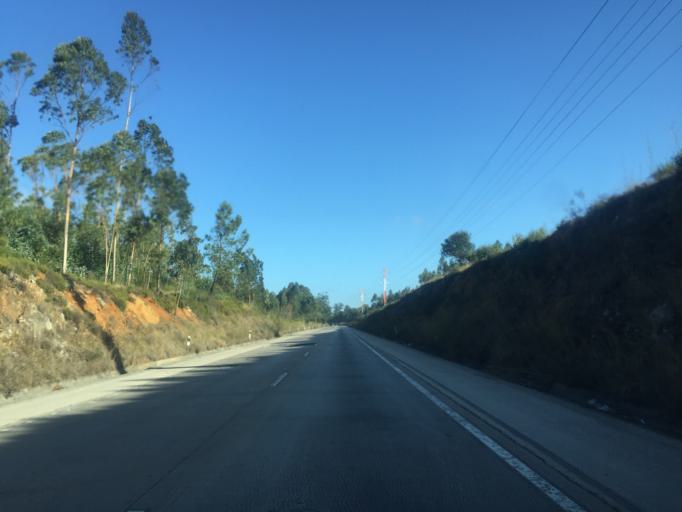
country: PT
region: Santarem
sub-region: Rio Maior
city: Rio Maior
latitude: 39.3561
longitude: -8.9701
